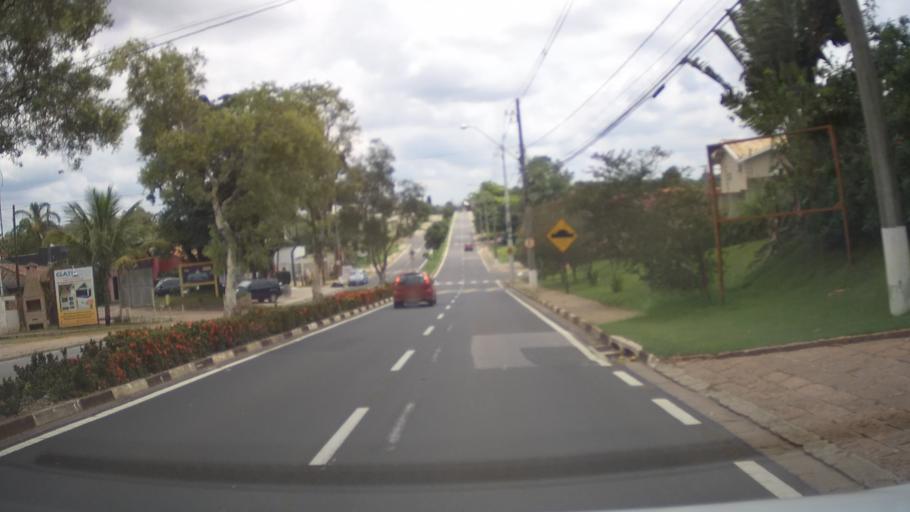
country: BR
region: Sao Paulo
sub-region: Vinhedo
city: Vinhedo
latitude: -23.0261
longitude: -46.9627
